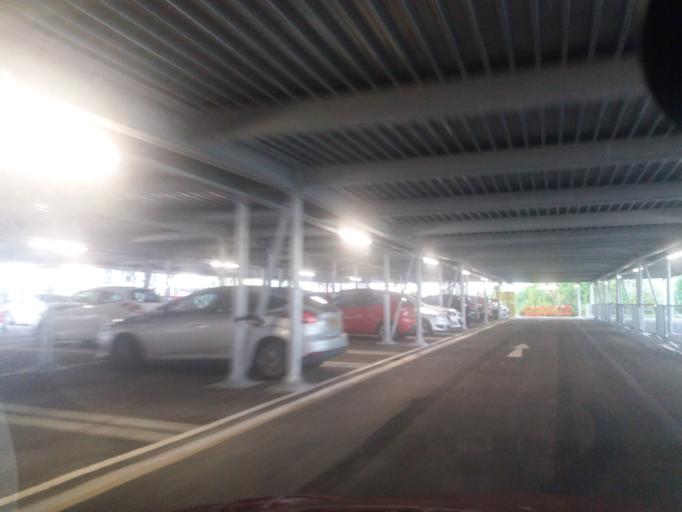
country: GB
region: England
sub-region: Lancashire
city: Chorley
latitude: 53.6547
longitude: -2.6269
